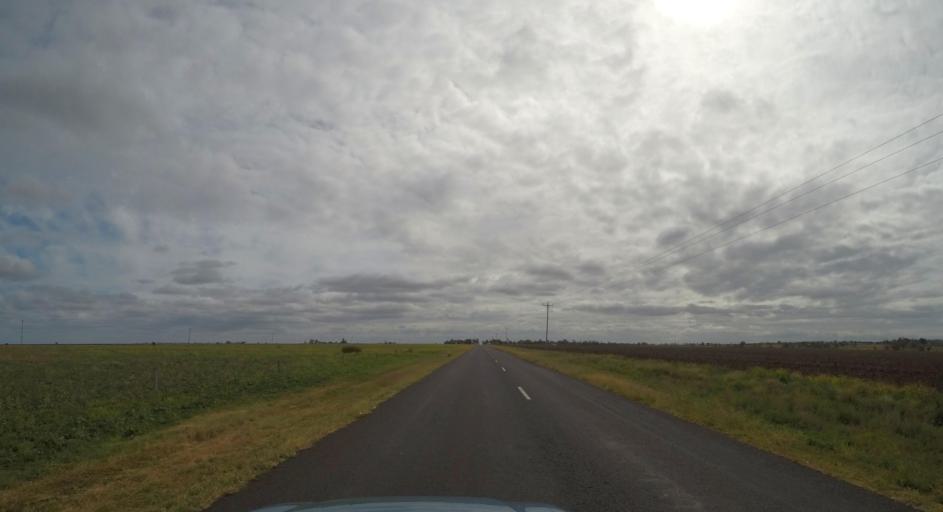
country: AU
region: Queensland
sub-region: Western Downs
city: Dalby
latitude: -26.9771
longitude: 151.2229
